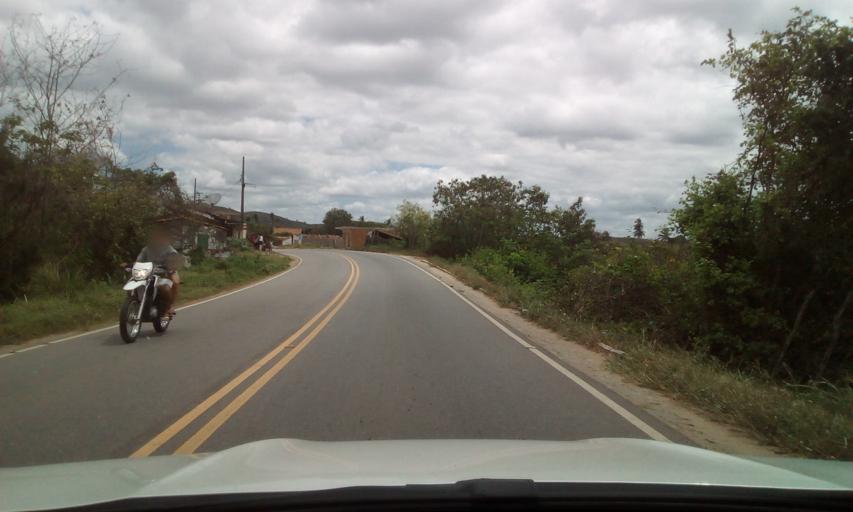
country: BR
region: Paraiba
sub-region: Serra Redonda
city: Alagoa Grande
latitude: -7.1642
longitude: -35.5924
